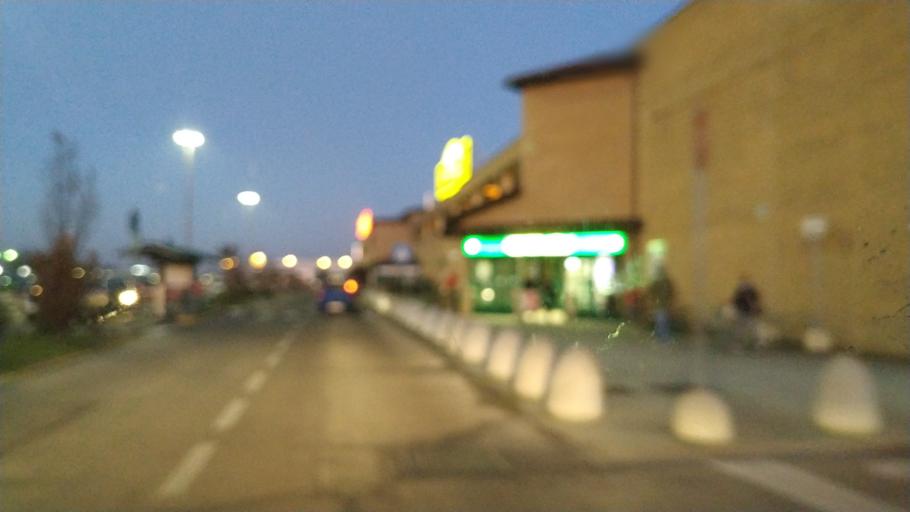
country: IT
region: Piedmont
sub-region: Provincia di Alessandria
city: Villanova Monferrato
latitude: 45.1677
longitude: 8.4656
